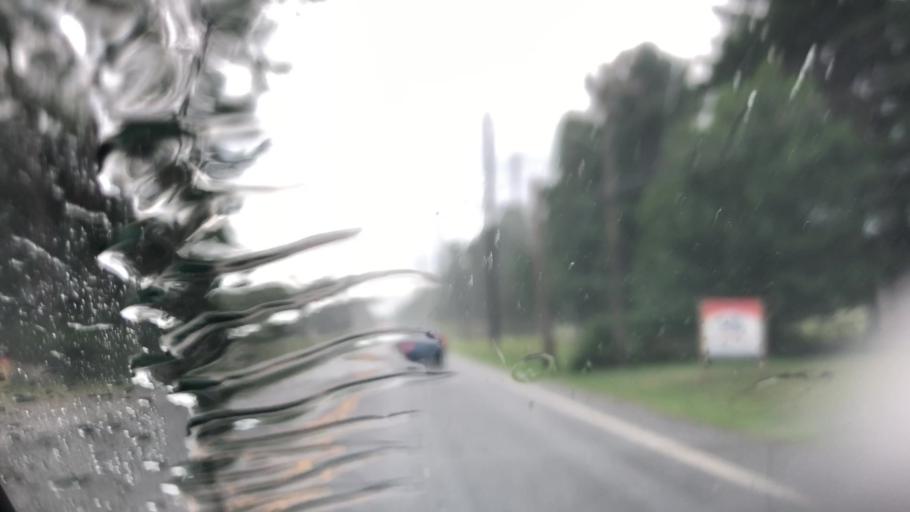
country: US
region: Ohio
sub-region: Stark County
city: Massillon
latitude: 40.8359
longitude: -81.5022
